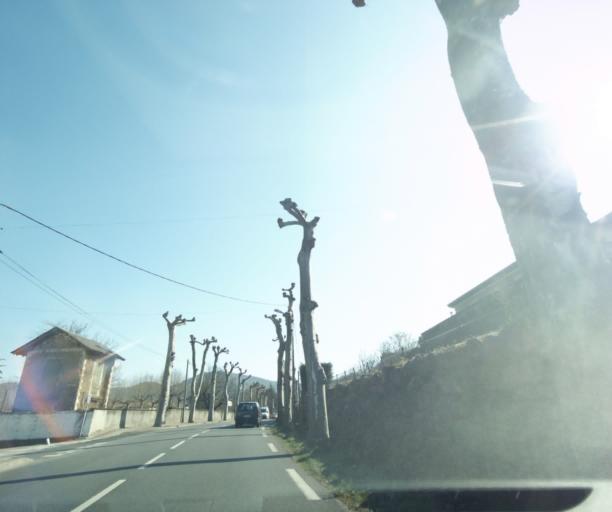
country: FR
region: Midi-Pyrenees
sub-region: Departement de l'Aveyron
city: Saint-Affrique
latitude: 43.9575
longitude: 2.8726
